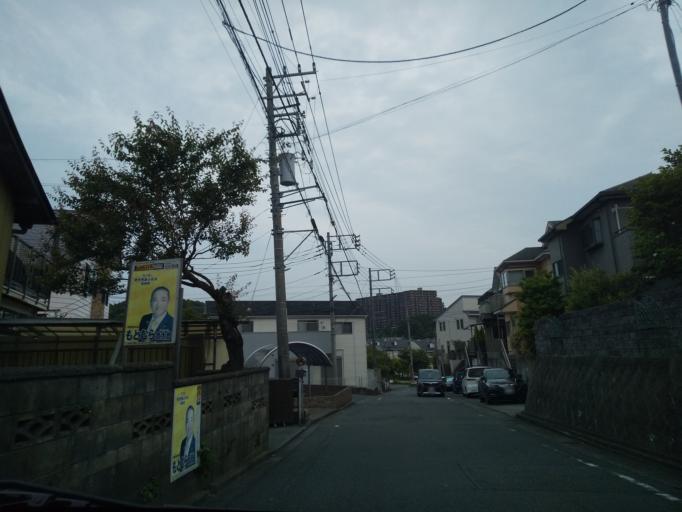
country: JP
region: Tokyo
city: Hachioji
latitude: 35.5979
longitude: 139.3584
